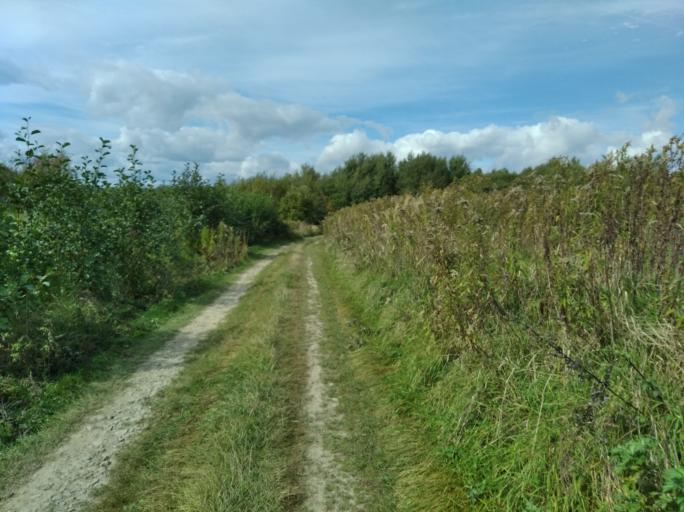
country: PL
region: Subcarpathian Voivodeship
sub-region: Powiat strzyzowski
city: Jawornik
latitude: 49.8455
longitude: 21.8613
